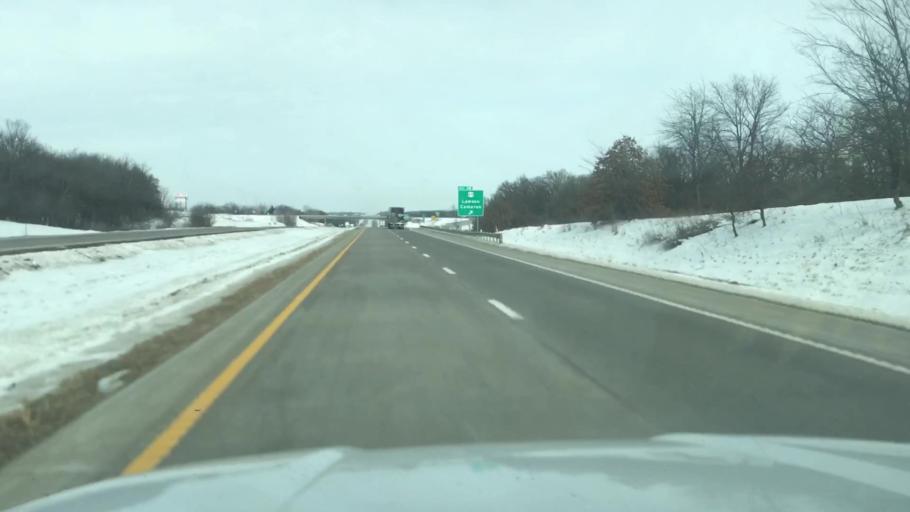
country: US
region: Missouri
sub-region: Clinton County
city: Cameron
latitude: 39.6631
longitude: -94.2368
